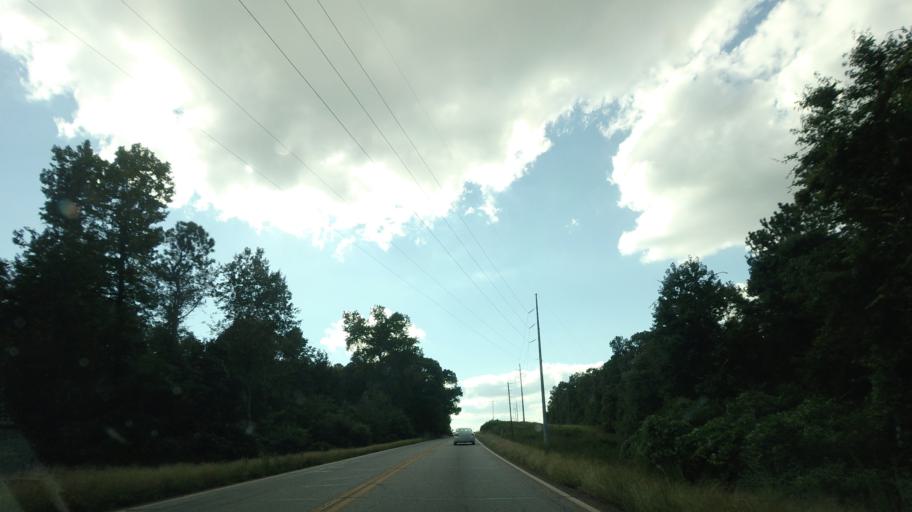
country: US
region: Georgia
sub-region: Lamar County
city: Barnesville
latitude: 33.0542
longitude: -84.0891
